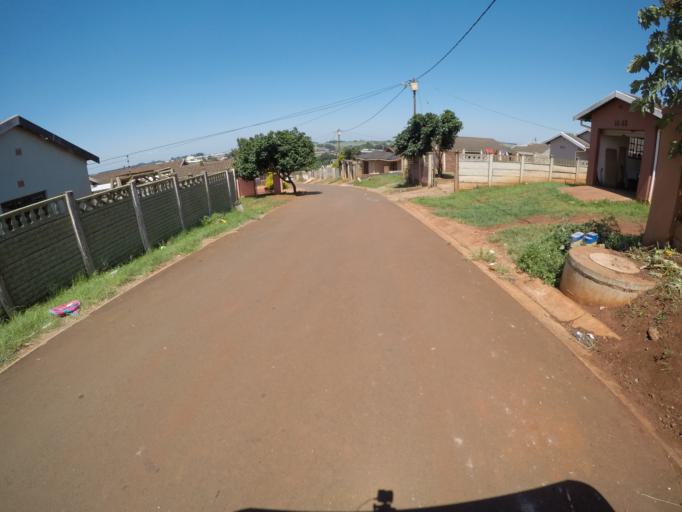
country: ZA
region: KwaZulu-Natal
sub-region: uThungulu District Municipality
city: Empangeni
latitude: -28.7732
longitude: 31.8816
